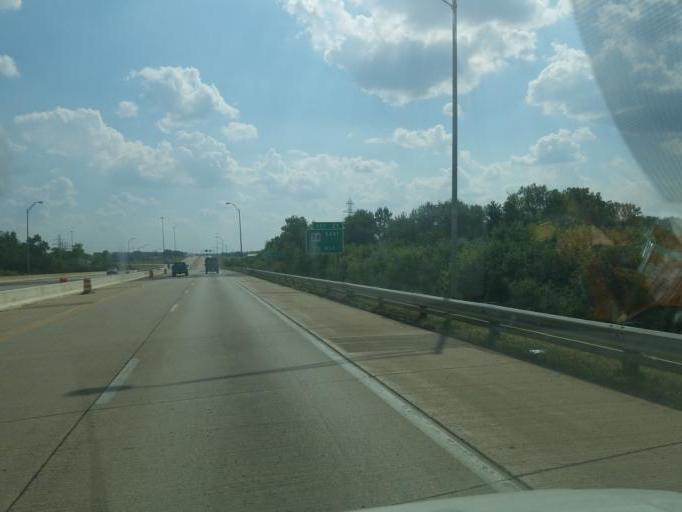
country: US
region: Indiana
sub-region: Allen County
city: New Haven
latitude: 41.0925
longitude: -84.9948
